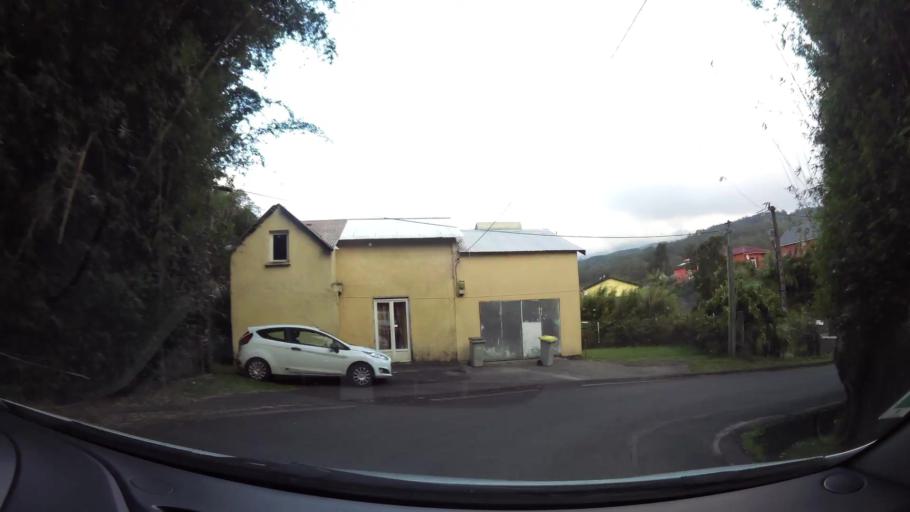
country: RE
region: Reunion
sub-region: Reunion
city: Saint-Denis
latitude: -20.9230
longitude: 55.4367
